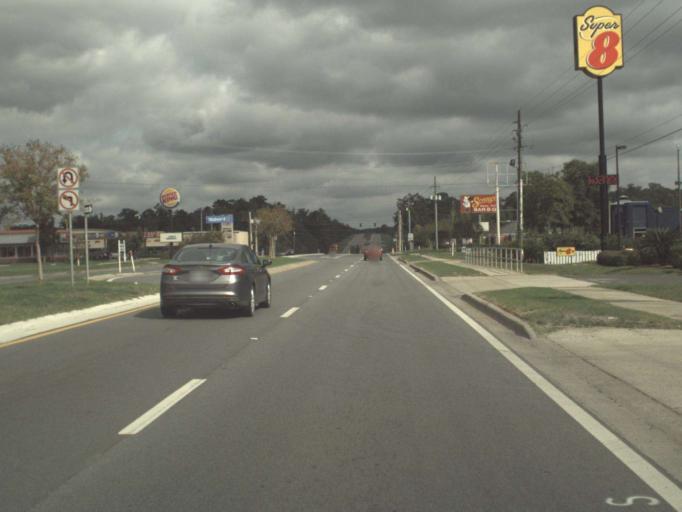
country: US
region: Florida
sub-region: Jackson County
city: Marianna
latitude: 30.7267
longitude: -85.1853
